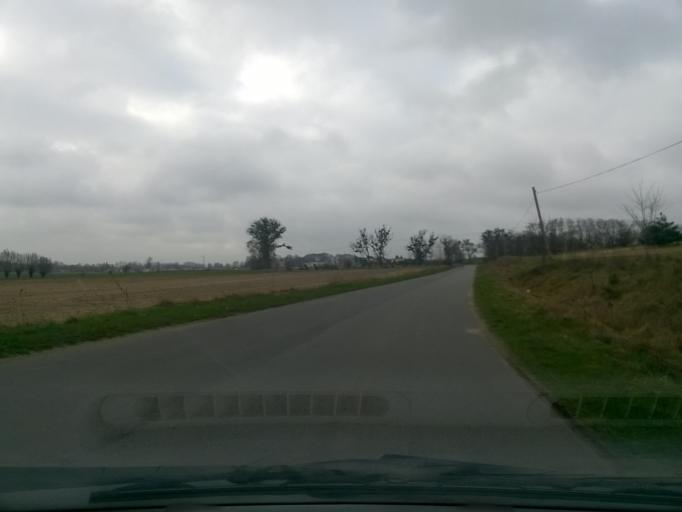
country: PL
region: Kujawsko-Pomorskie
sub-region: Powiat nakielski
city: Szubin
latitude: 52.9674
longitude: 17.6260
